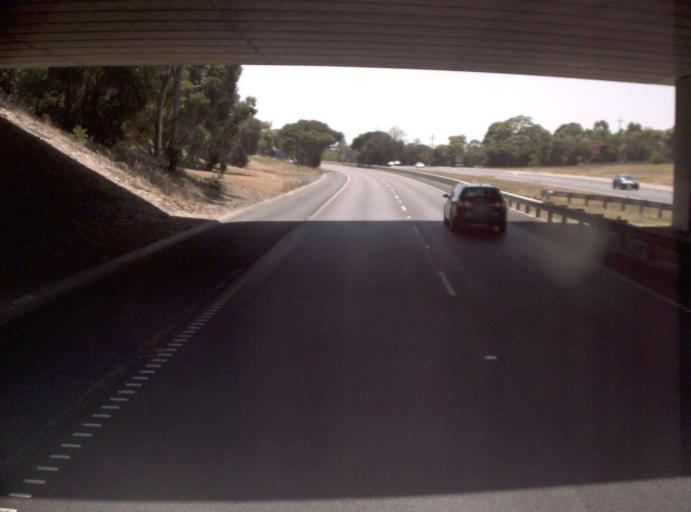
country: AU
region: Victoria
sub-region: Frankston
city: Seaford
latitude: -38.1089
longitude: 145.1390
